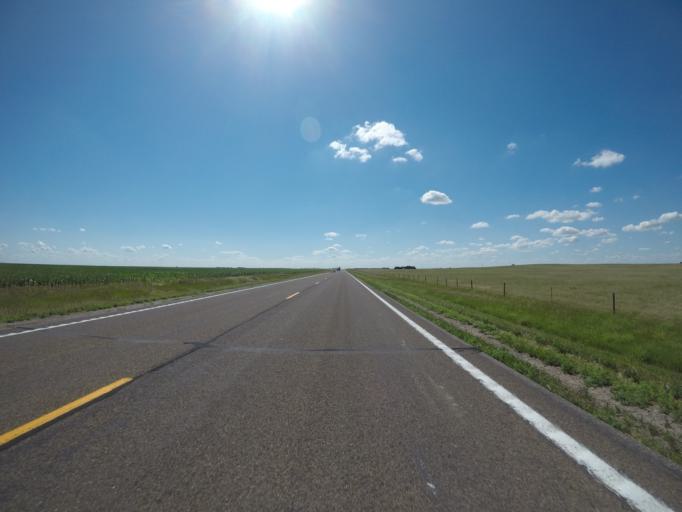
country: US
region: Nebraska
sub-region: Chase County
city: Imperial
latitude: 40.5377
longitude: -101.8660
